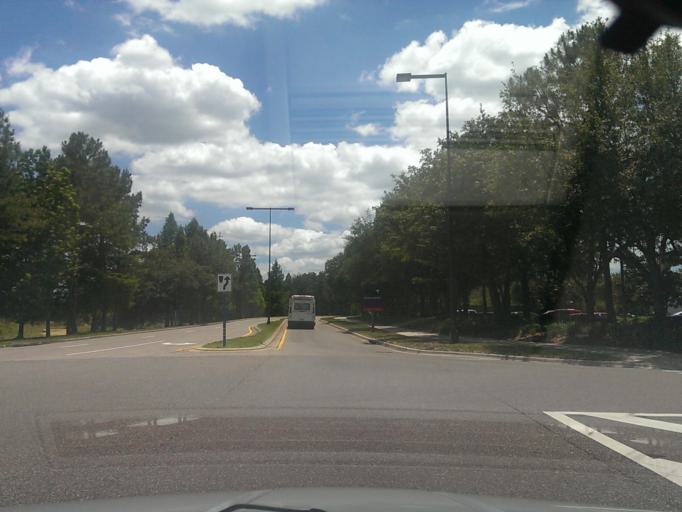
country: US
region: Florida
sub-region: Osceola County
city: Celebration
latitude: 28.3398
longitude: -81.5713
